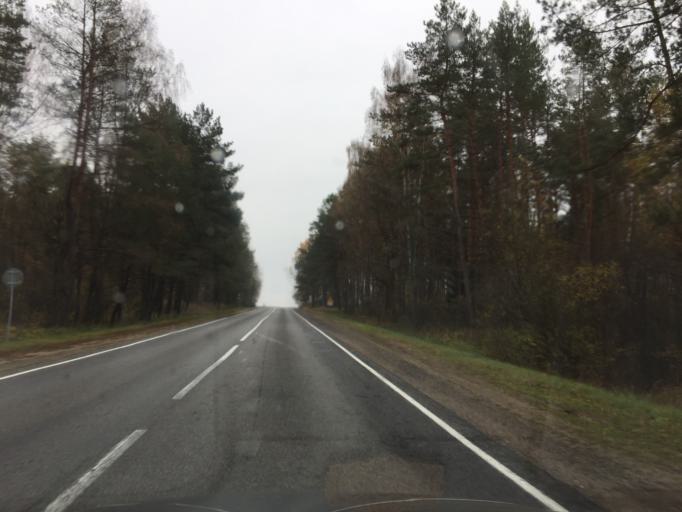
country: BY
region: Mogilev
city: Cherykaw
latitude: 53.6362
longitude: 31.2799
